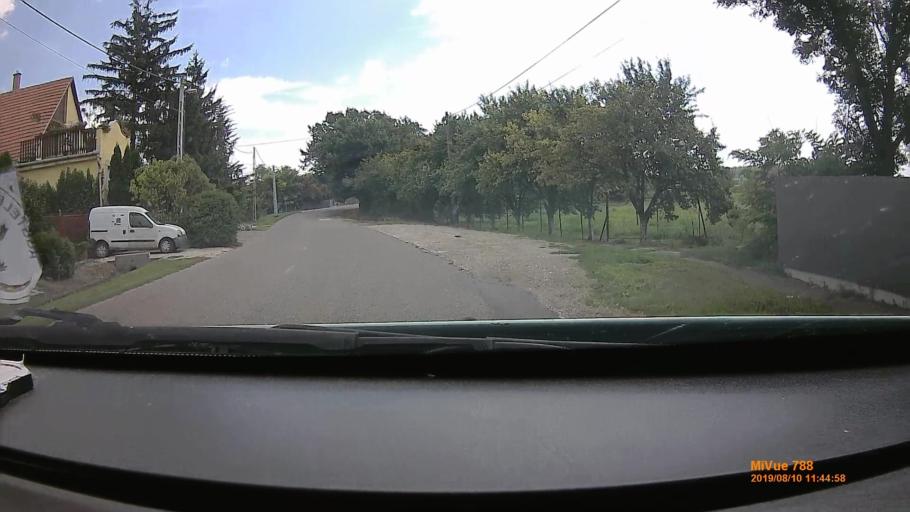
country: HU
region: Borsod-Abauj-Zemplen
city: Szentistvan
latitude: 47.7190
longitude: 20.6243
